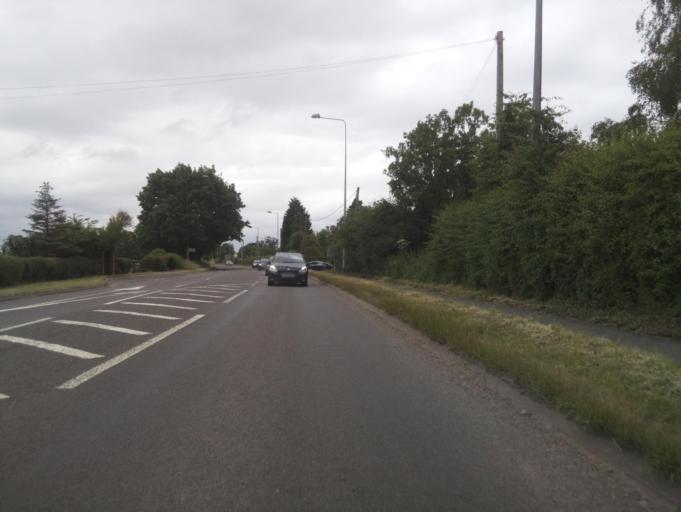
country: GB
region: England
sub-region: Staffordshire
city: Penkridge
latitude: 52.7098
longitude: -2.1233
